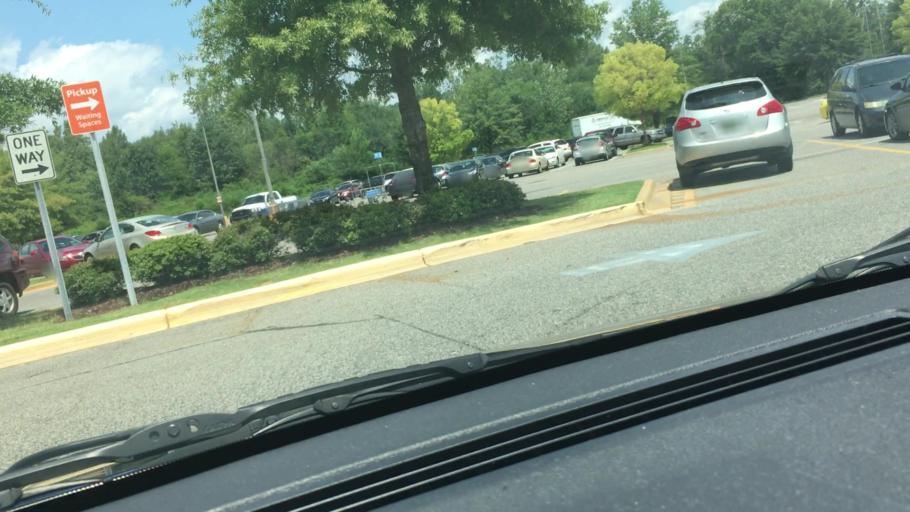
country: US
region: Alabama
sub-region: Tuscaloosa County
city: Northport
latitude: 33.2362
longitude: -87.6133
